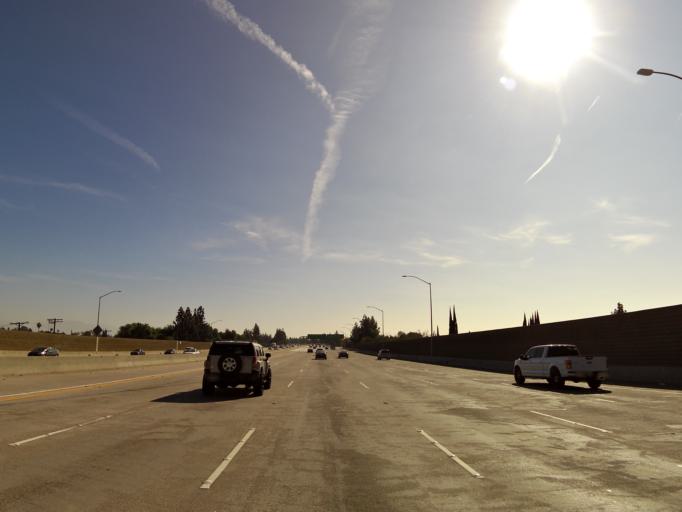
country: US
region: California
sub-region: Los Angeles County
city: San Fernando
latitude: 34.2720
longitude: -118.4902
